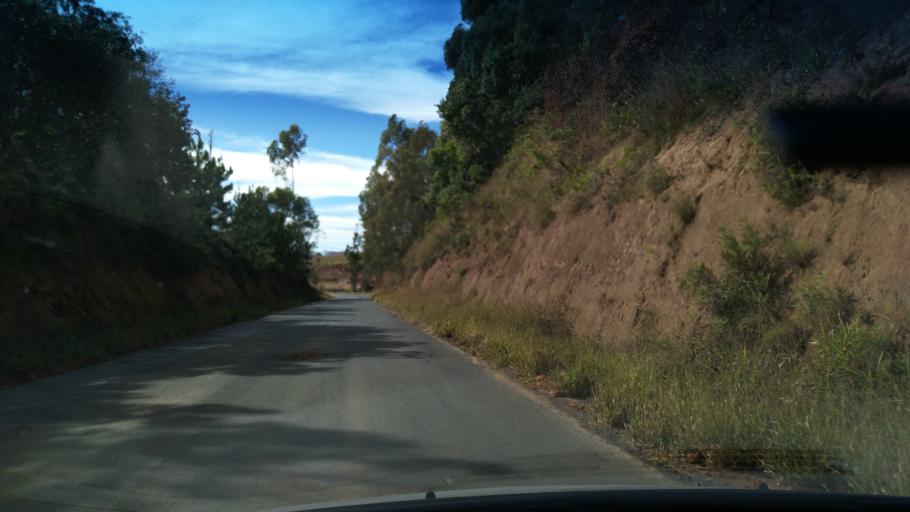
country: BR
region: Minas Gerais
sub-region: Andradas
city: Andradas
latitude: -22.0428
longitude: -46.3347
